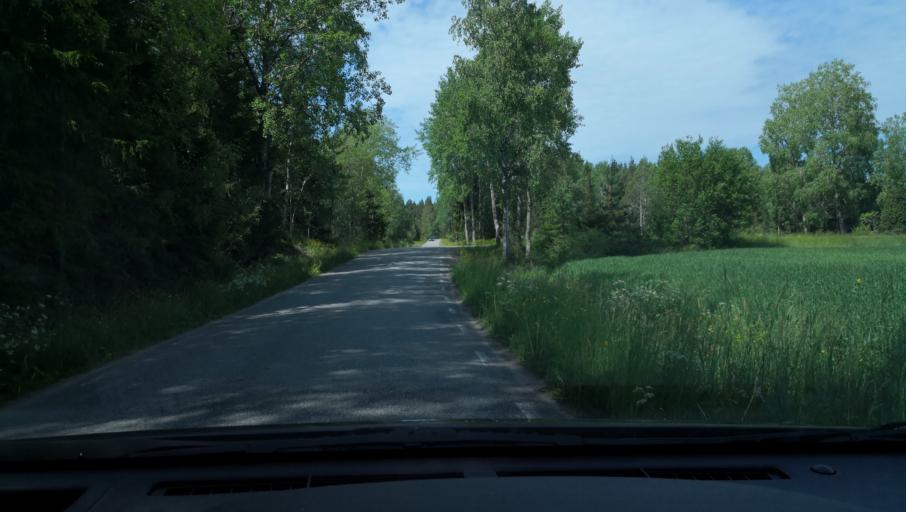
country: SE
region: Stockholm
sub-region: Sigtuna Kommun
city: Sigtuna
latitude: 59.6869
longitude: 17.6688
